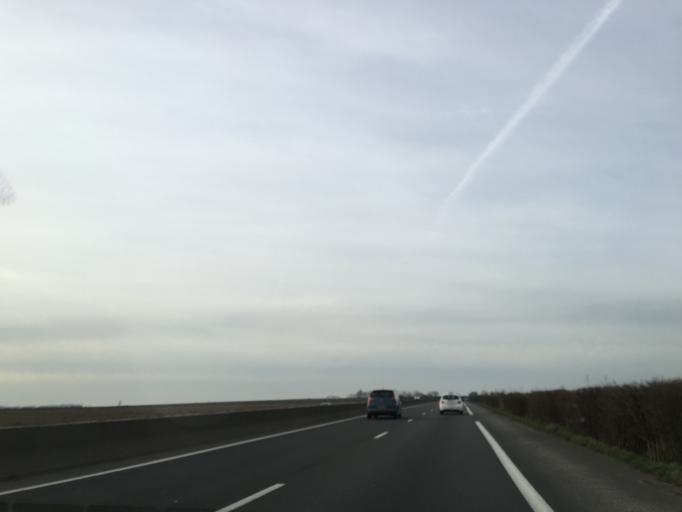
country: FR
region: Nord-Pas-de-Calais
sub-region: Departement du Pas-de-Calais
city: Bailleul-Sir-Berthoult
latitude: 50.3261
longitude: 2.8693
